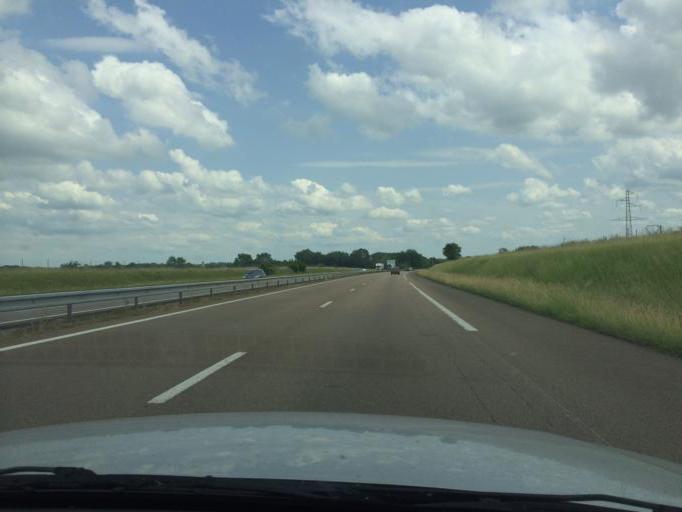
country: FR
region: Champagne-Ardenne
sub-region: Departement de la Marne
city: Sillery
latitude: 49.1997
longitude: 4.1103
